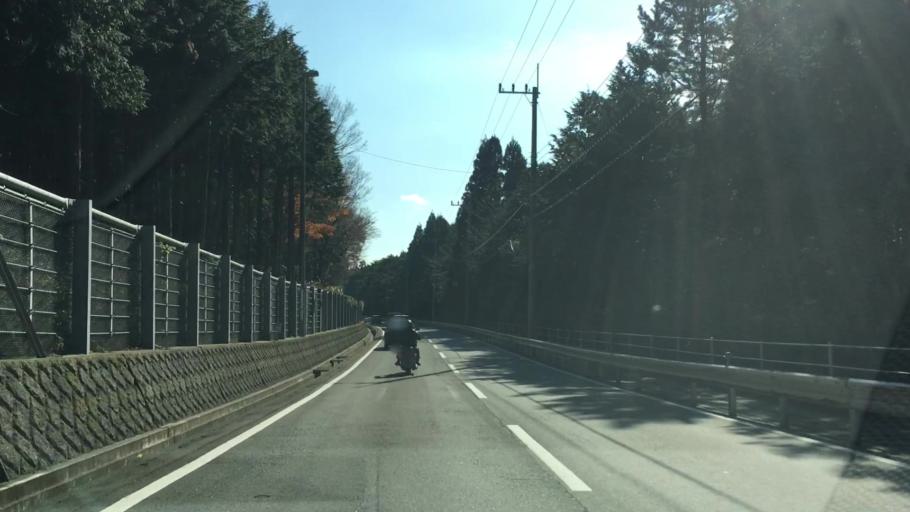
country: JP
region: Shizuoka
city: Gotemba
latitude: 35.3791
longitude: 138.8584
